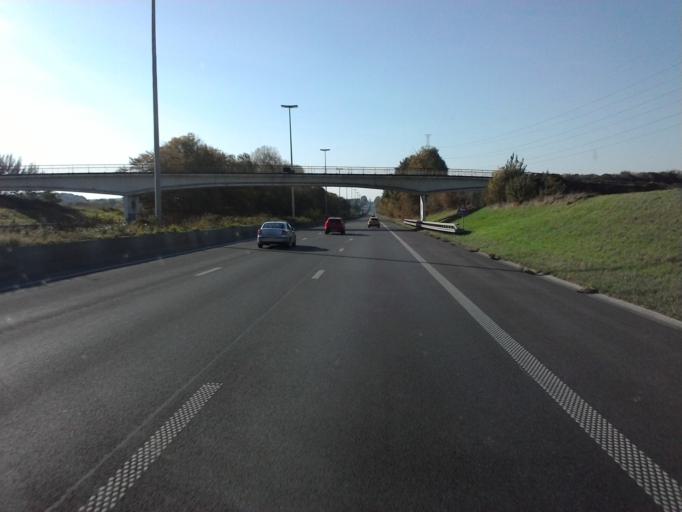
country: BE
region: Wallonia
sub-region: Province de Namur
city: Gembloux
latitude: 50.4944
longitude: 4.6832
